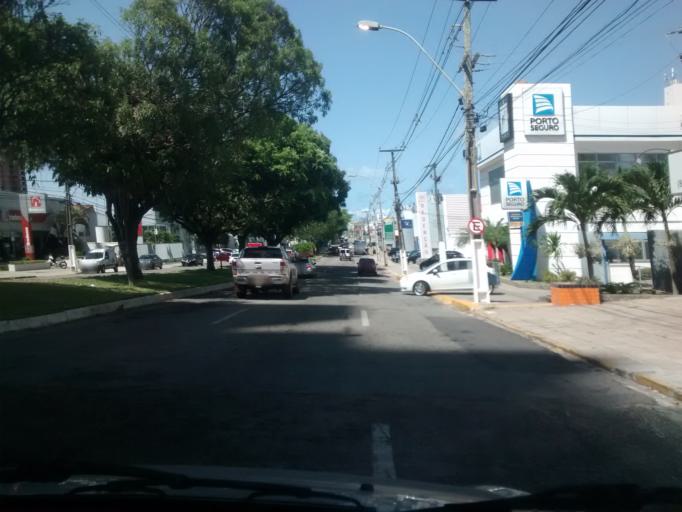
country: BR
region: Rio Grande do Norte
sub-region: Natal
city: Natal
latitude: -5.8180
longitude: -35.2123
